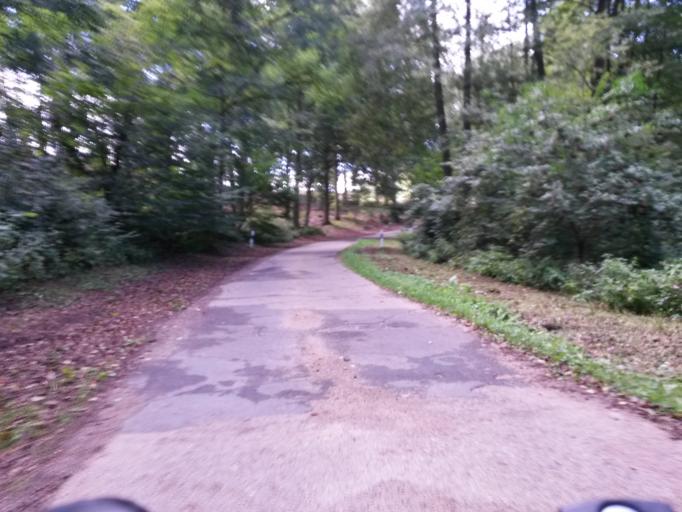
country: DE
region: Brandenburg
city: Mittenwalde
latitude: 53.1755
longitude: 13.6033
